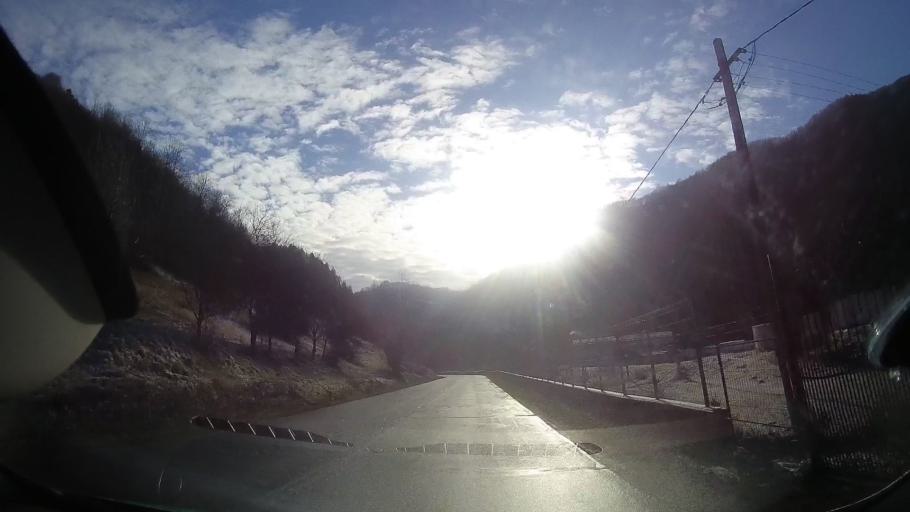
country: RO
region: Alba
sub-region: Comuna Sohodol
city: Sohodol
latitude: 46.3601
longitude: 23.0214
